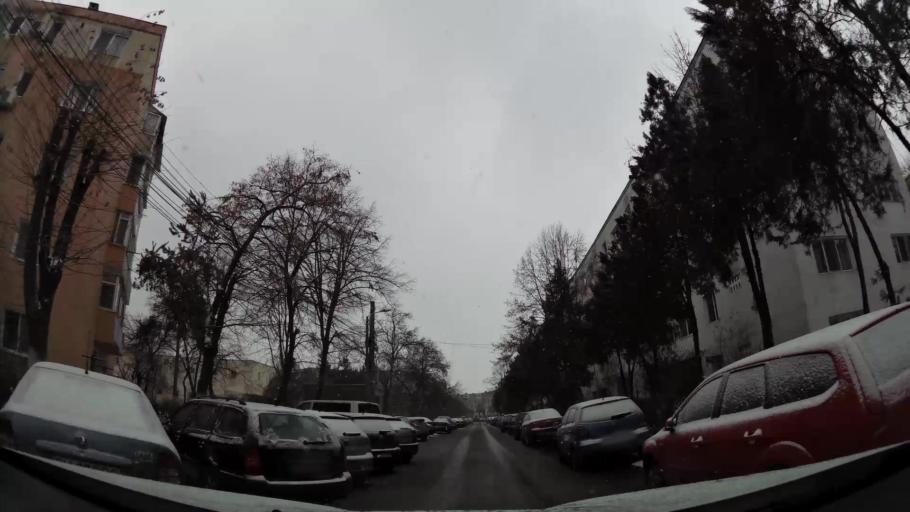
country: RO
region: Prahova
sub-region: Comuna Targsoru Vechi
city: Strejnicu
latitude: 44.9350
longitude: 25.9827
